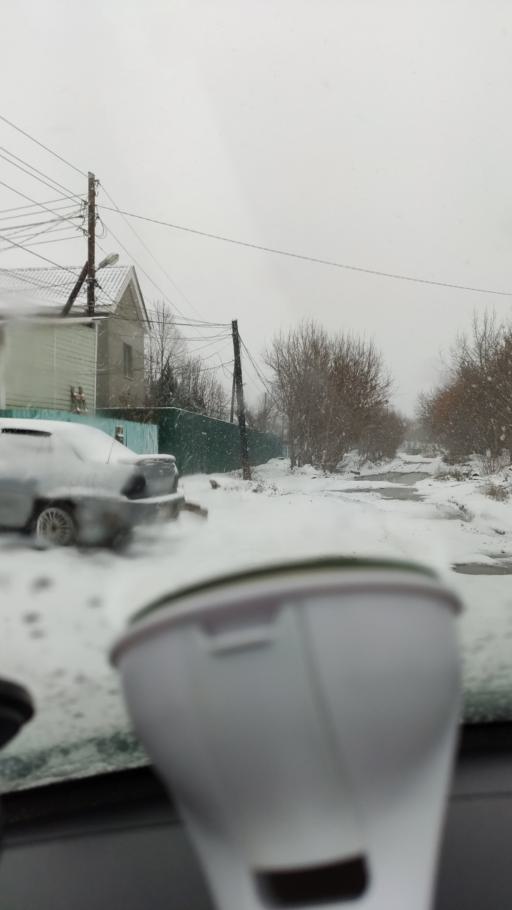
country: RU
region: Samara
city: Samara
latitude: 53.1795
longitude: 50.1608
